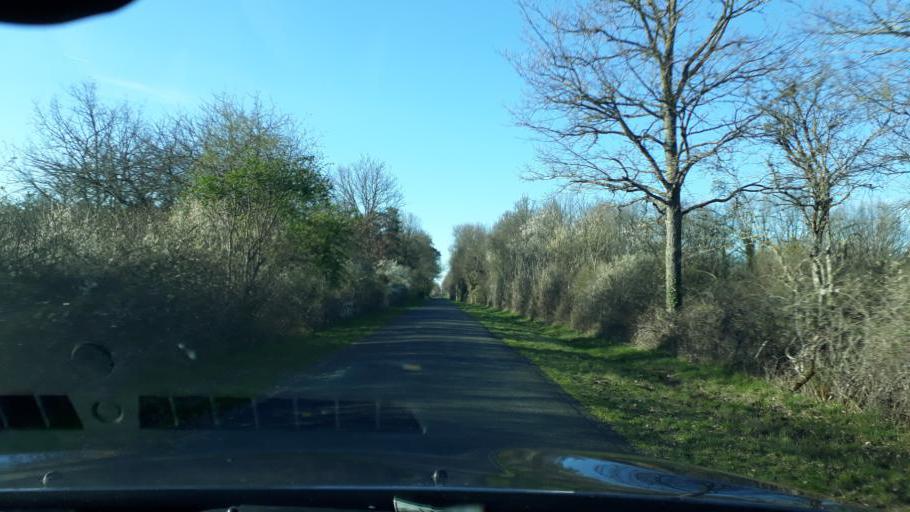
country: FR
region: Centre
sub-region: Departement du Loiret
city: Jouy-le-Potier
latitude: 47.7312
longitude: 1.8226
